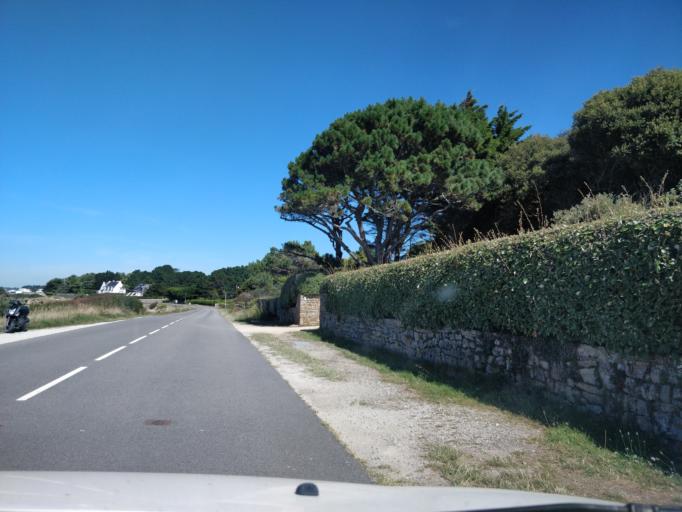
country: FR
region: Brittany
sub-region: Departement du Morbihan
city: Saint-Philibert
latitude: 47.5694
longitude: -3.0072
